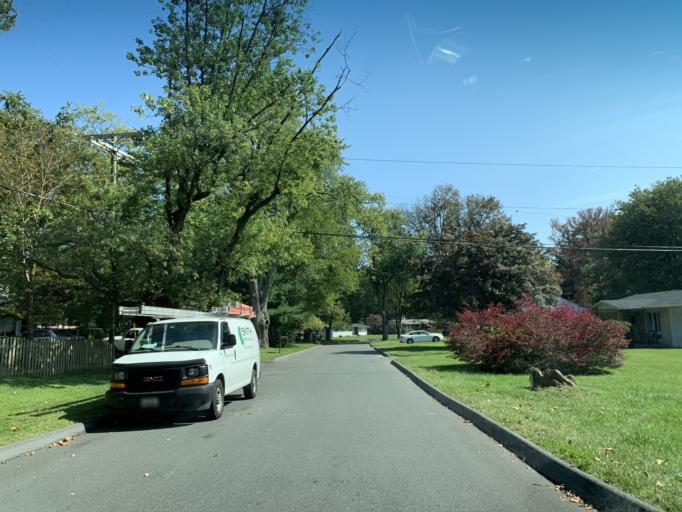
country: US
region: Maryland
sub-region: Harford County
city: South Bel Air
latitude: 39.5215
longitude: -76.3396
